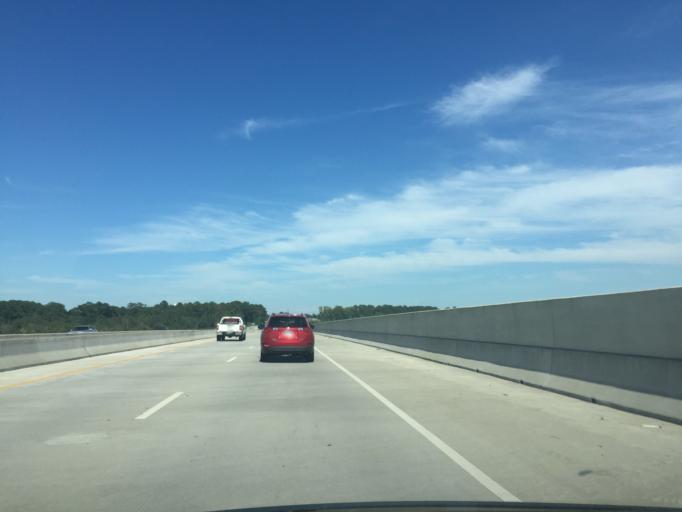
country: US
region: Georgia
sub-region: Chatham County
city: Montgomery
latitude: 31.9752
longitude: -81.1189
